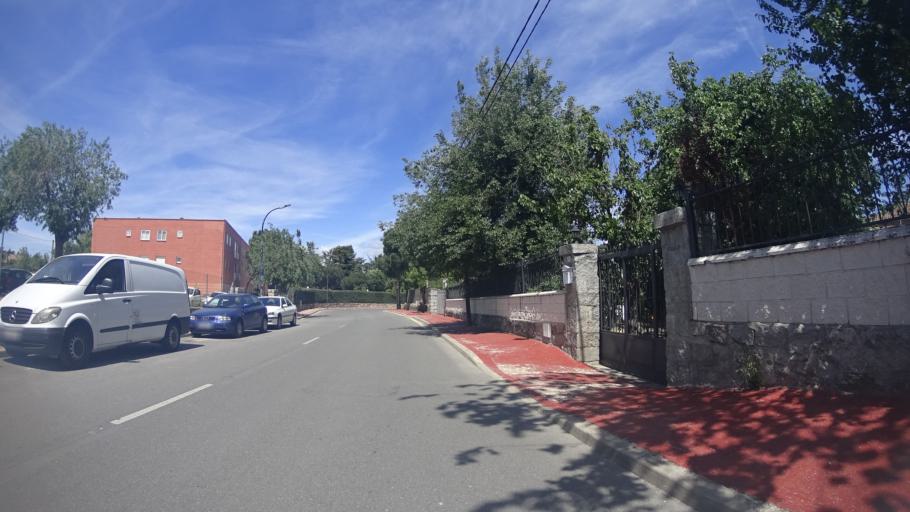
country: ES
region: Madrid
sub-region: Provincia de Madrid
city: Galapagar
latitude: 40.5726
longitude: -4.0045
